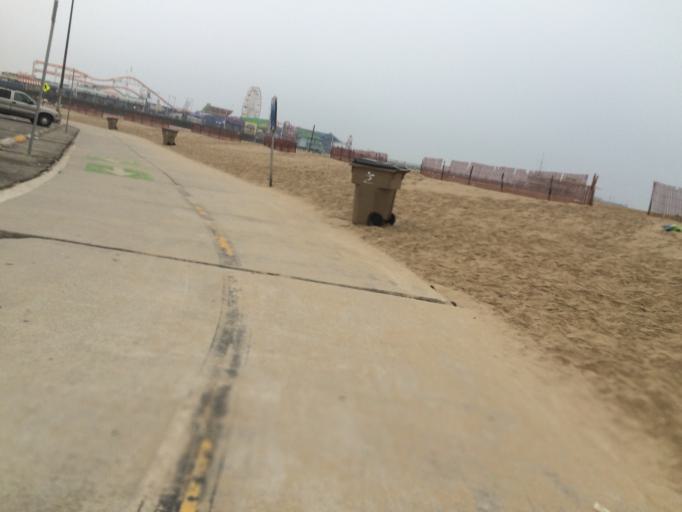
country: US
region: California
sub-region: Los Angeles County
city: Santa Monica
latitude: 34.0109
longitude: -118.4987
